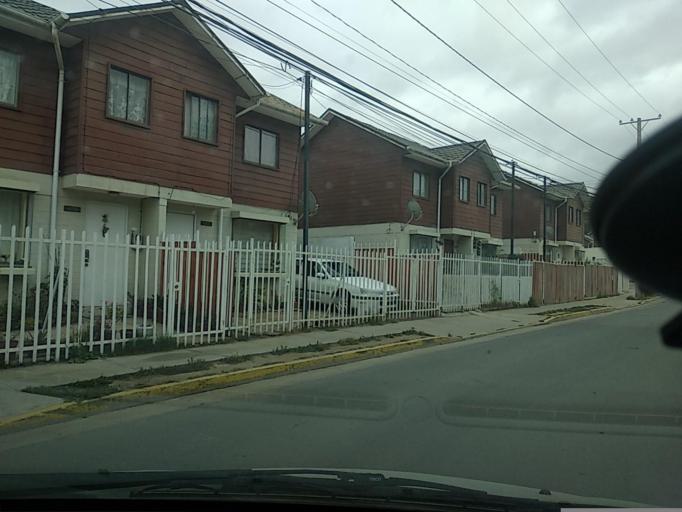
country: CL
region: Valparaiso
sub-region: Provincia de Marga Marga
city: Villa Alemana
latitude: -33.0371
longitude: -71.3589
